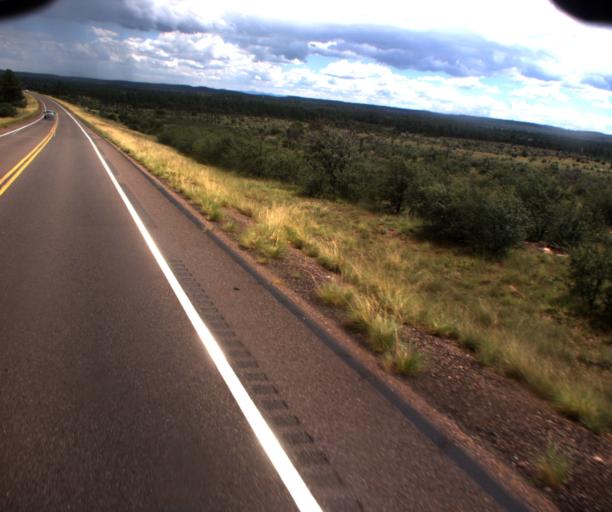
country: US
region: Arizona
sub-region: Navajo County
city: Linden
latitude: 34.3645
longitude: -110.3502
